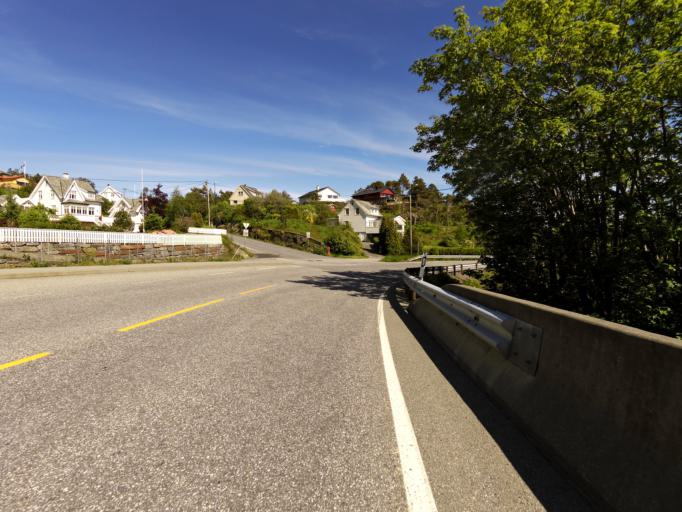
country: NO
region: Hordaland
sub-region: Stord
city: Sagvag
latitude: 59.7813
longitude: 5.3880
